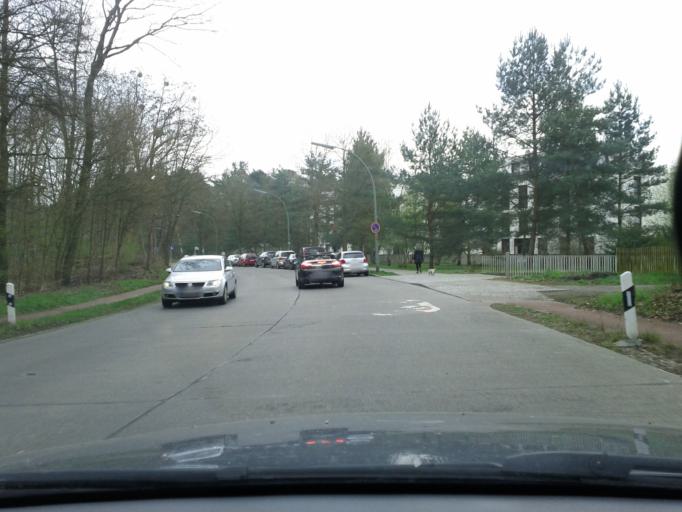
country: DE
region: Berlin
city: Dahlem
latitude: 52.4585
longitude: 13.2623
